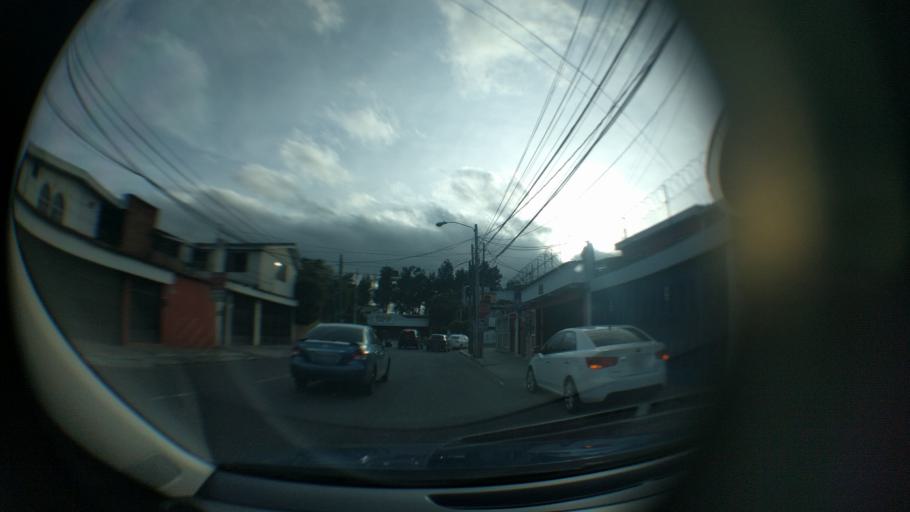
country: GT
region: Guatemala
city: Guatemala City
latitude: 14.5951
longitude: -90.5553
